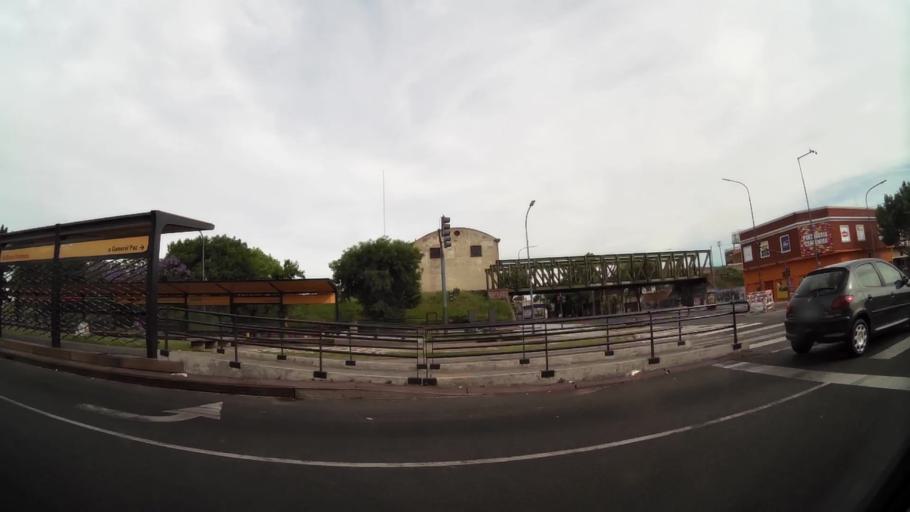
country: AR
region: Buenos Aires F.D.
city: Villa Lugano
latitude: -34.6477
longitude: -58.4284
